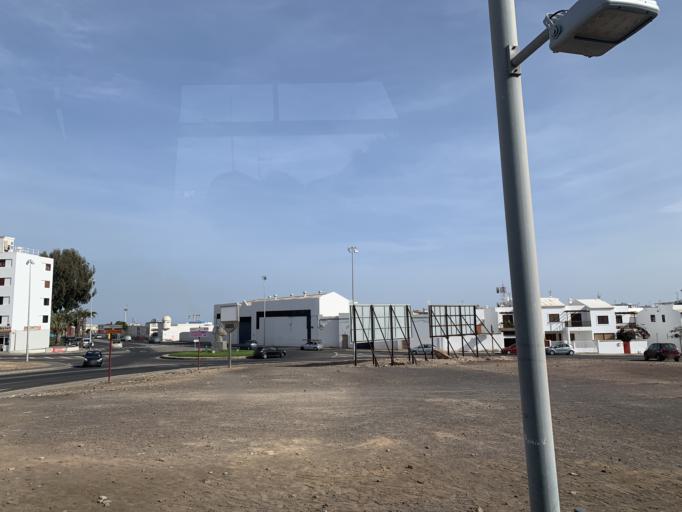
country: ES
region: Canary Islands
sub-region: Provincia de Las Palmas
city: Puerto del Rosario
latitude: 28.5037
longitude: -13.8593
